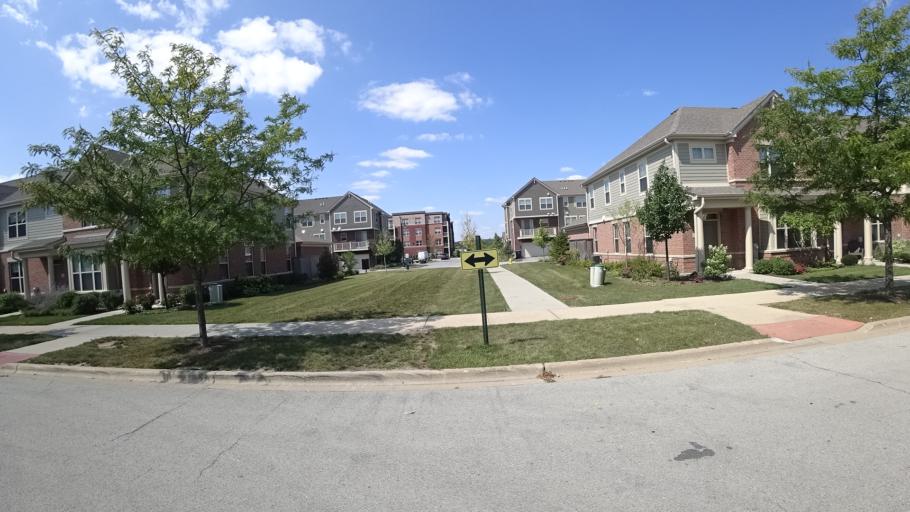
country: US
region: Illinois
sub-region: Cook County
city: Orland Park
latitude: 41.6357
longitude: -87.8504
